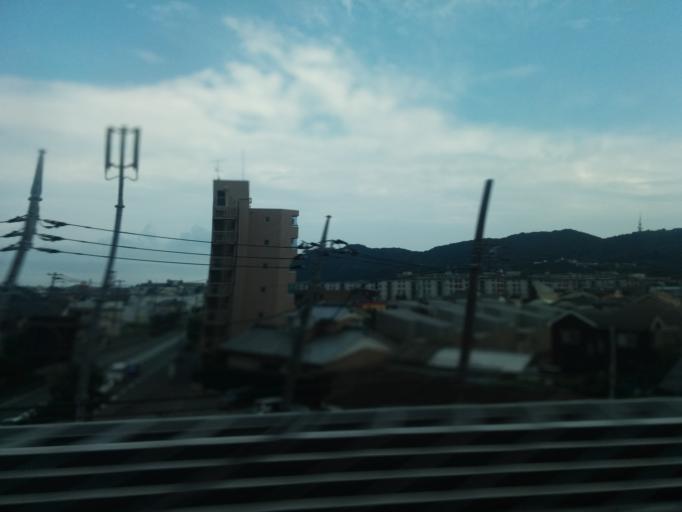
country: JP
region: Kanagawa
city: Oiso
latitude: 35.3387
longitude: 139.3041
